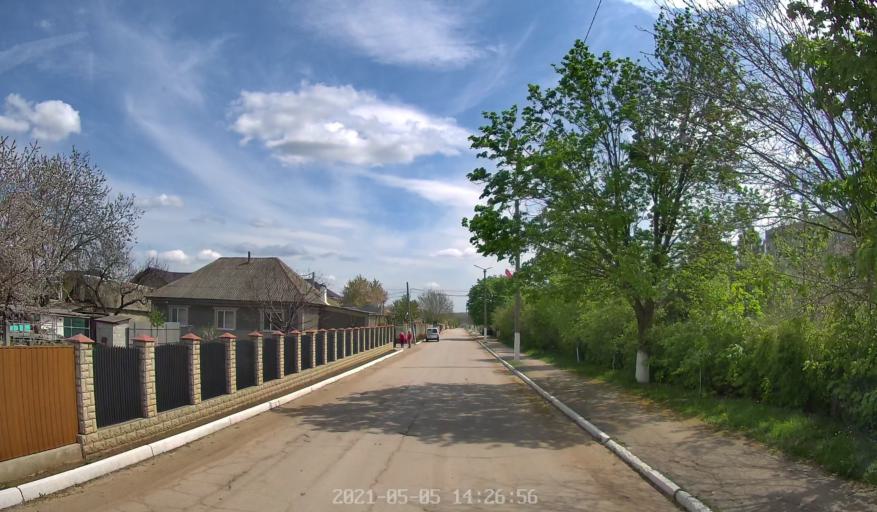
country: MD
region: Chisinau
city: Vadul lui Voda
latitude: 47.0791
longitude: 29.1394
